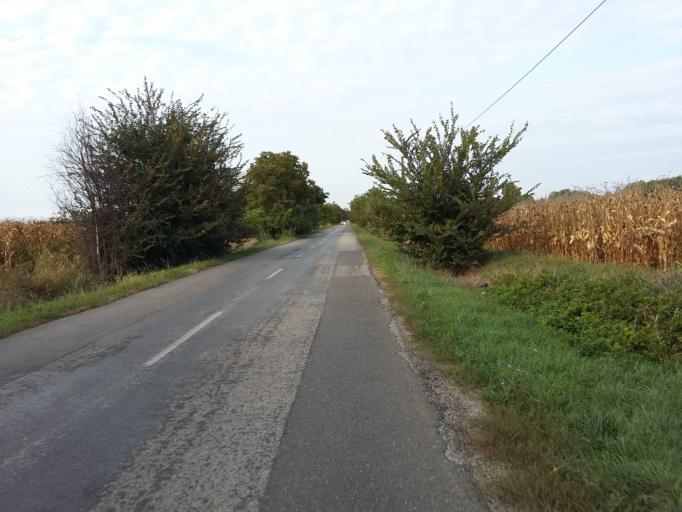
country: HU
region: Csongrad
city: Szeged
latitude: 46.2139
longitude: 20.1091
